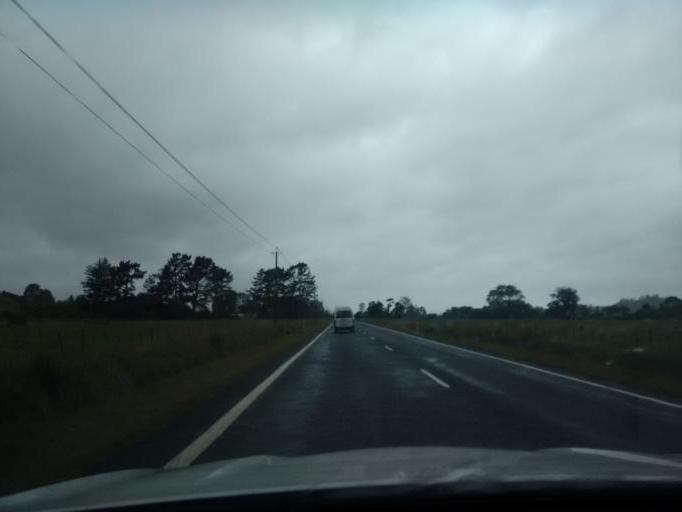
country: NZ
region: Waikato
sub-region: Thames-Coromandel District
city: Whitianga
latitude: -36.8545
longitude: 175.6536
